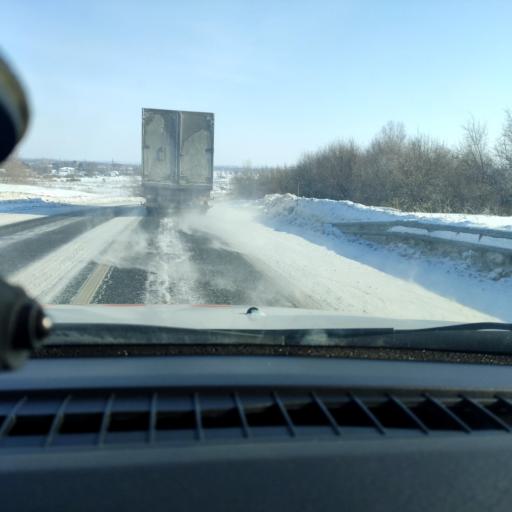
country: RU
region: Samara
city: Smyshlyayevka
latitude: 53.1562
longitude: 50.4038
